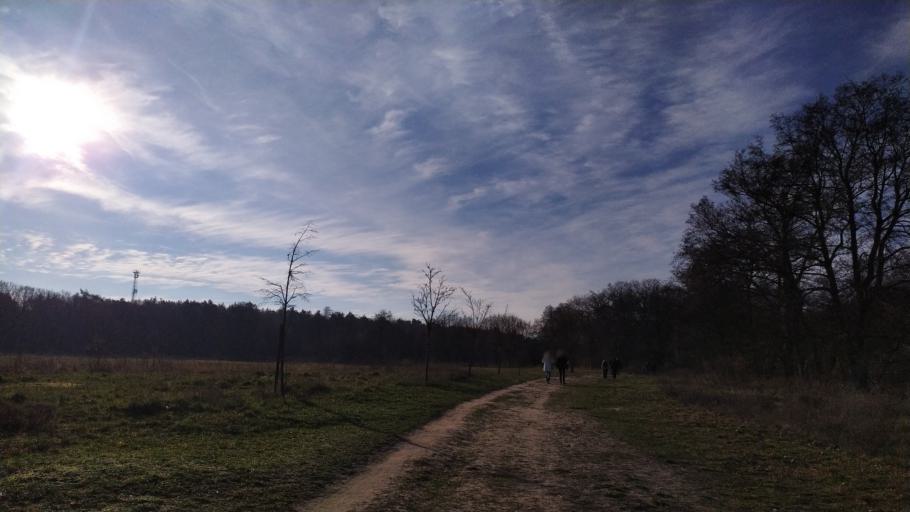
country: DE
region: Berlin
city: Friedrichshagen
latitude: 52.4789
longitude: 13.6361
